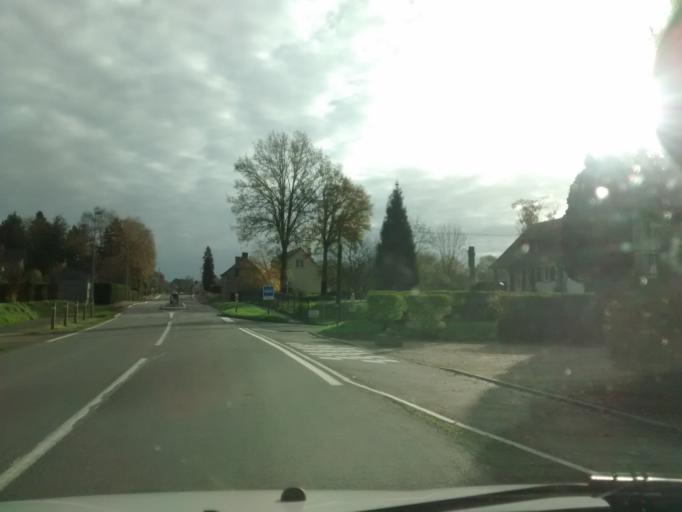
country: FR
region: Brittany
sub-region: Departement d'Ille-et-Vilaine
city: Montreuil-sous-Perouse
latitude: 48.1428
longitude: -1.2514
